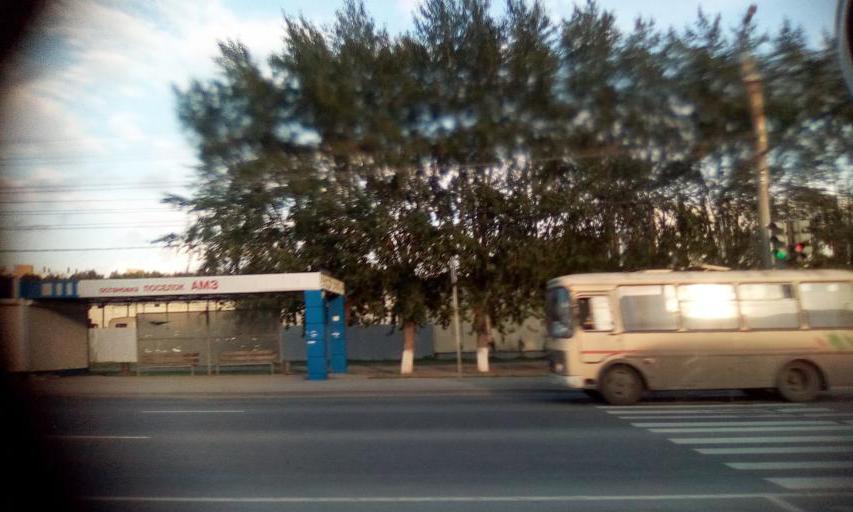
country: RU
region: Chelyabinsk
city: Novosineglazovskiy
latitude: 55.1152
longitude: 61.3591
